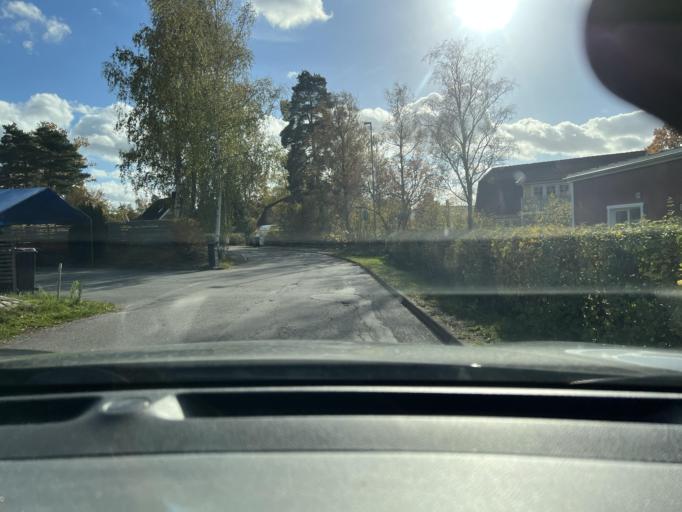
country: SE
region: Stockholm
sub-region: Vallentuna Kommun
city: Vallentuna
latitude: 59.5015
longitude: 18.0827
